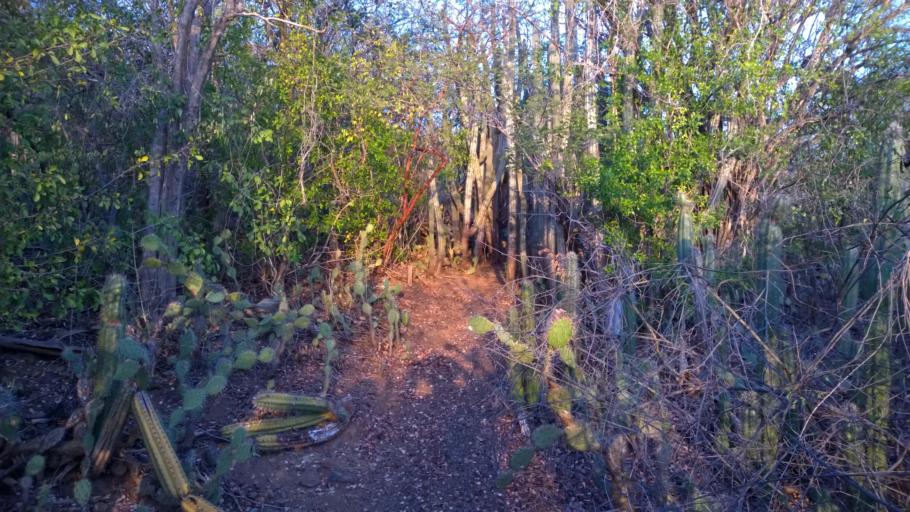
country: CW
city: Dorp Soto
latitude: 12.2594
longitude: -69.1086
